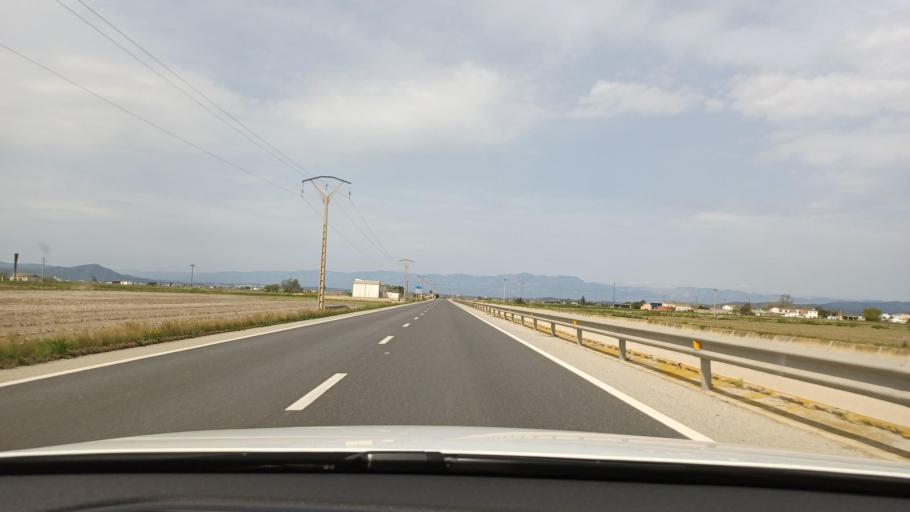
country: ES
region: Catalonia
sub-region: Provincia de Tarragona
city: Deltebre
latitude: 40.7090
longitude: 0.6883
